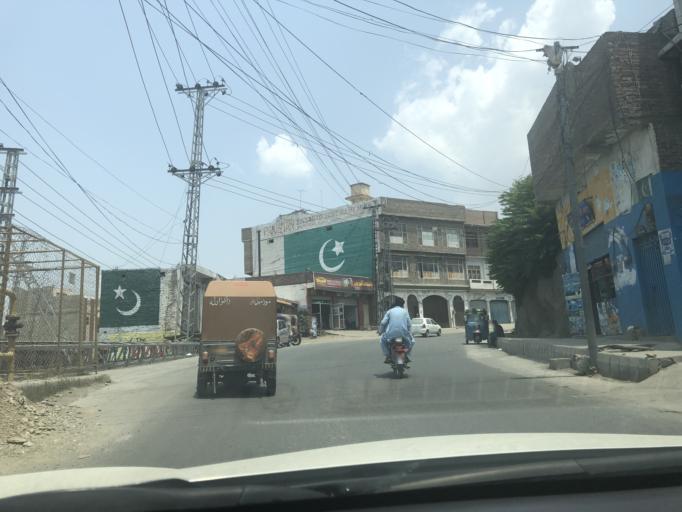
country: PK
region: Khyber Pakhtunkhwa
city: Mingora
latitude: 34.7718
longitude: 72.3486
